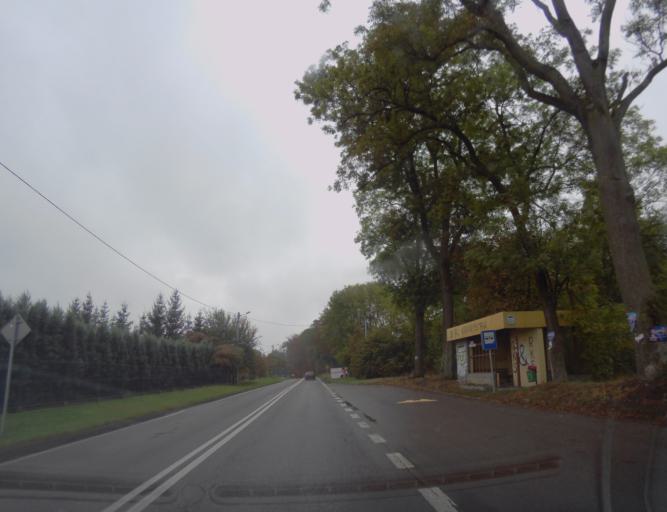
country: PL
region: Lublin Voivodeship
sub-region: Powiat krasnostawski
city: Krasnystaw
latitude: 51.0289
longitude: 23.2254
